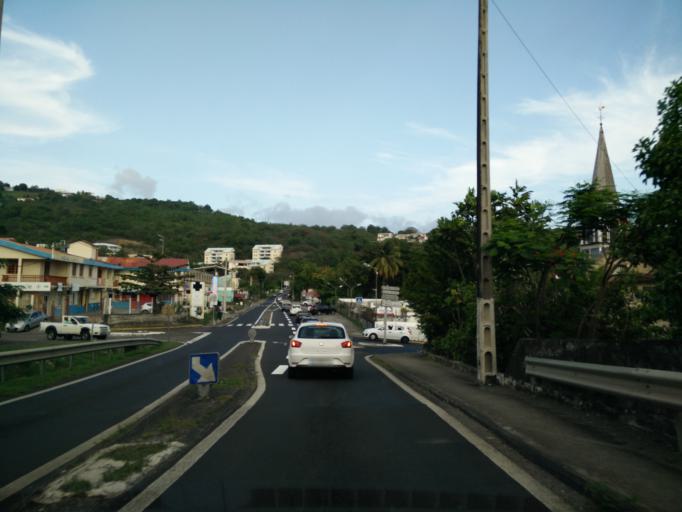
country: MQ
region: Martinique
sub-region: Martinique
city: Fort-de-France
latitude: 14.6440
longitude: -61.1385
